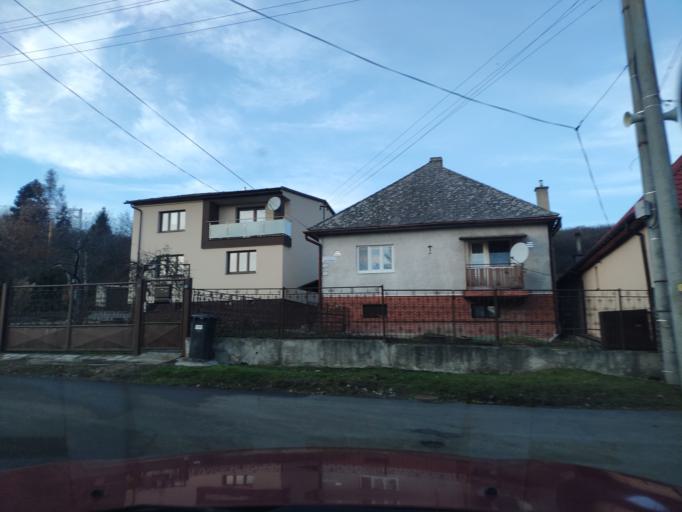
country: SK
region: Kosicky
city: Secovce
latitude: 48.6350
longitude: 21.4672
